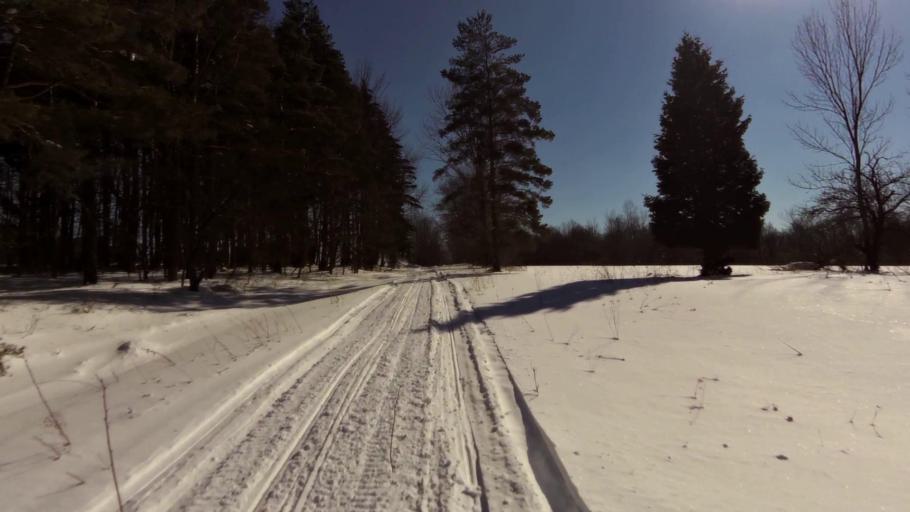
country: US
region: New York
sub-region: Cattaraugus County
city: Franklinville
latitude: 42.3489
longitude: -78.3244
